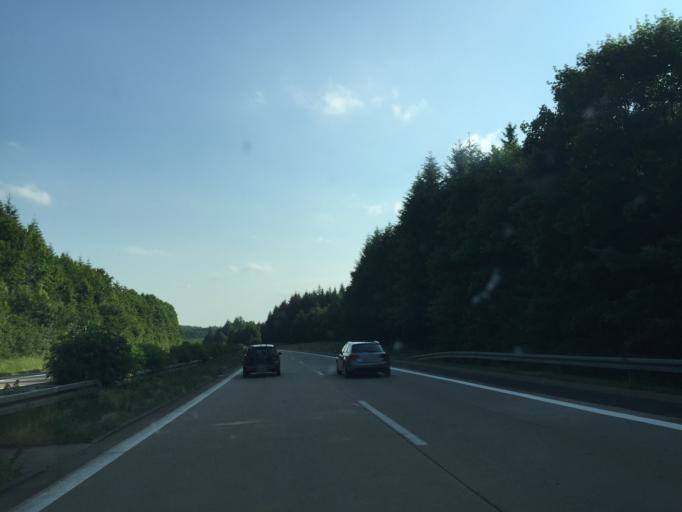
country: DE
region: Baden-Wuerttemberg
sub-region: Karlsruhe Region
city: Rosenberg
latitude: 49.4460
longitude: 9.5174
